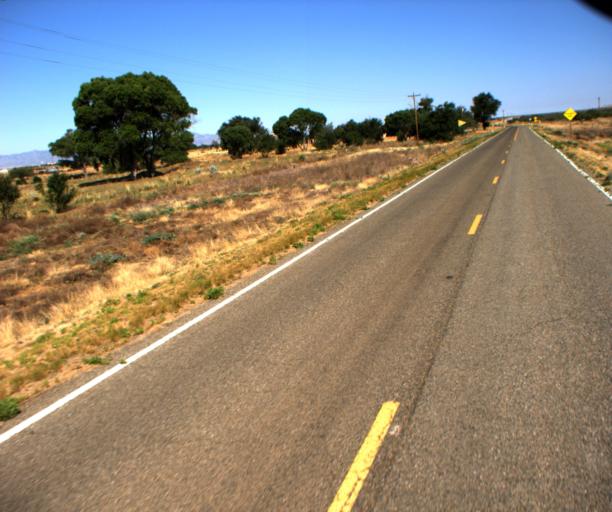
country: US
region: Arizona
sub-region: Graham County
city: Swift Trail Junction
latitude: 32.5882
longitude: -109.9666
